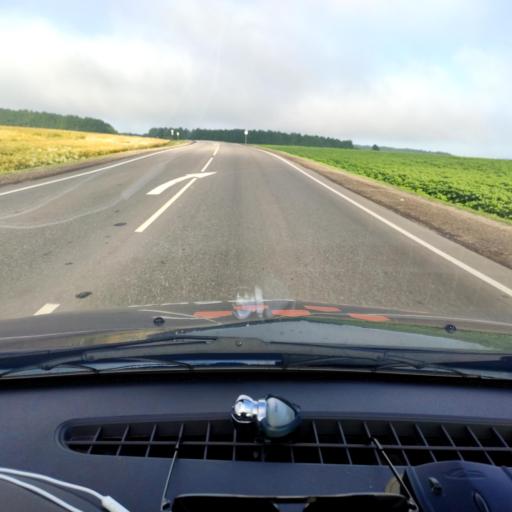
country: RU
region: Orjol
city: Livny
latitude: 52.4475
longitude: 37.4609
